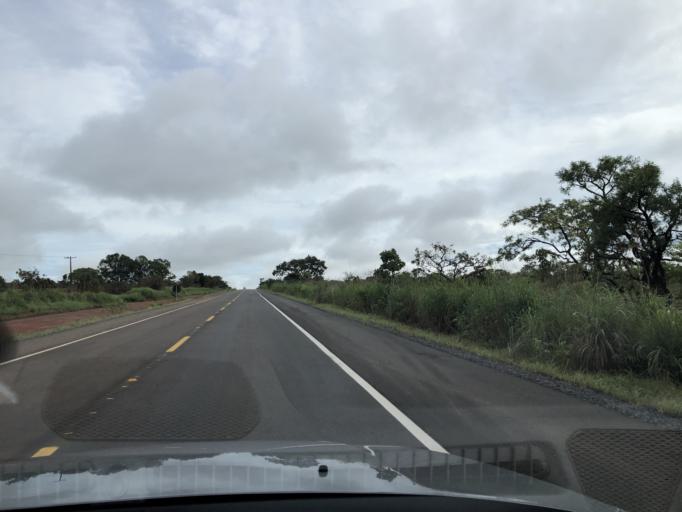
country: BR
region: Federal District
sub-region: Brasilia
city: Brasilia
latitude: -15.6395
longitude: -48.0787
